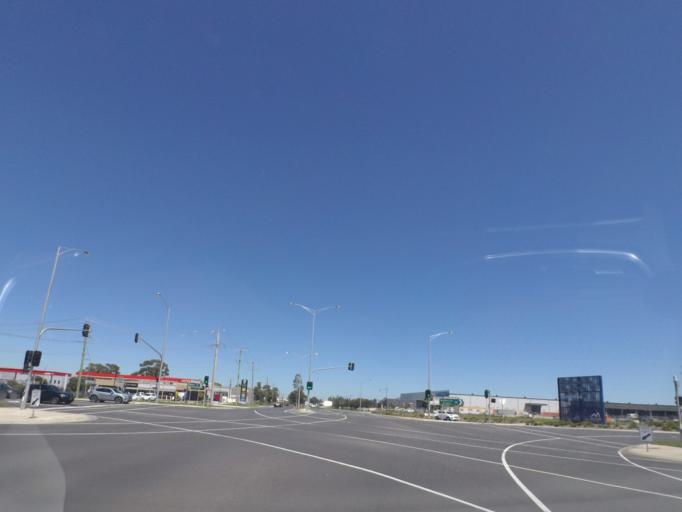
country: AU
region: Victoria
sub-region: Hume
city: Tullamarine
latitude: -37.7069
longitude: 144.8678
